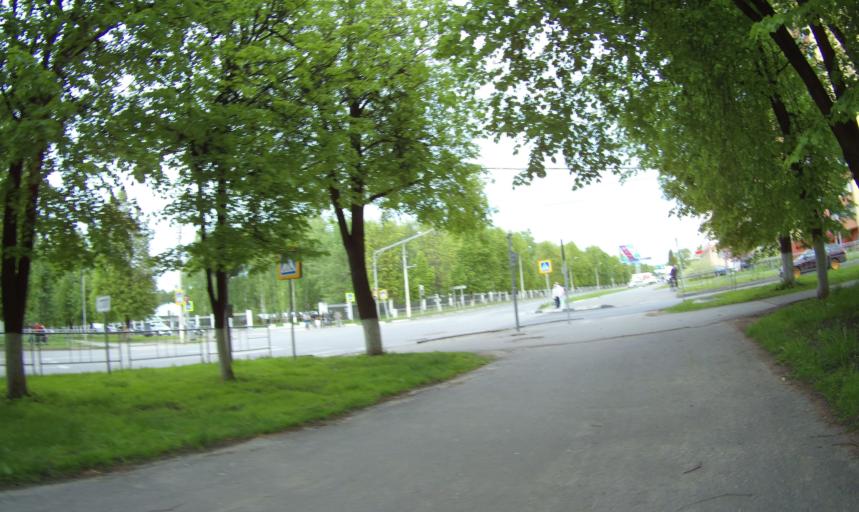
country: RU
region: Moskovskaya
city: Kolomna
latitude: 55.0854
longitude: 38.7735
